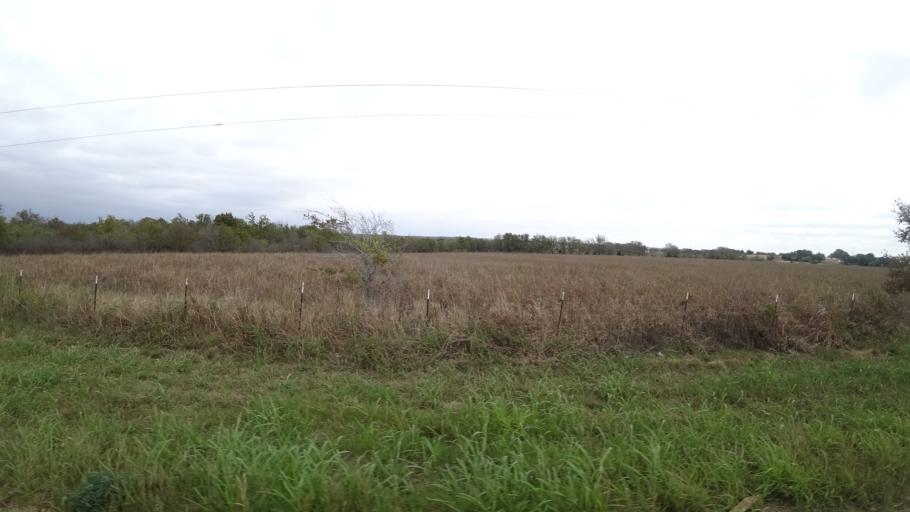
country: US
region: Texas
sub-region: Travis County
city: Manor
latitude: 30.3704
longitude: -97.5694
